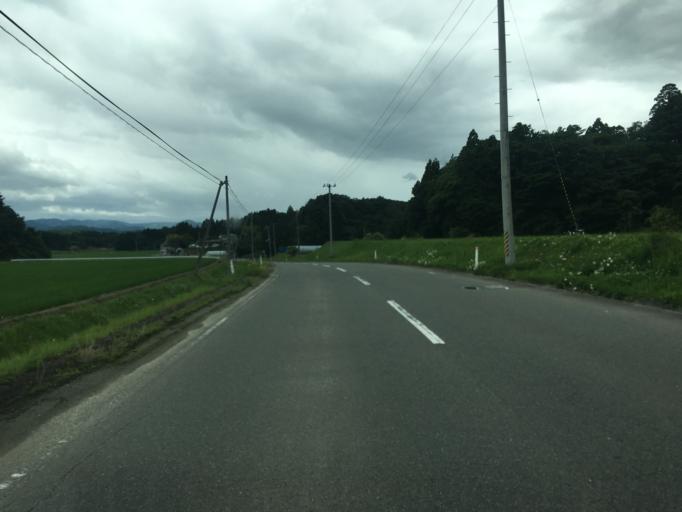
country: JP
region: Fukushima
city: Namie
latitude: 37.7416
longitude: 140.9782
